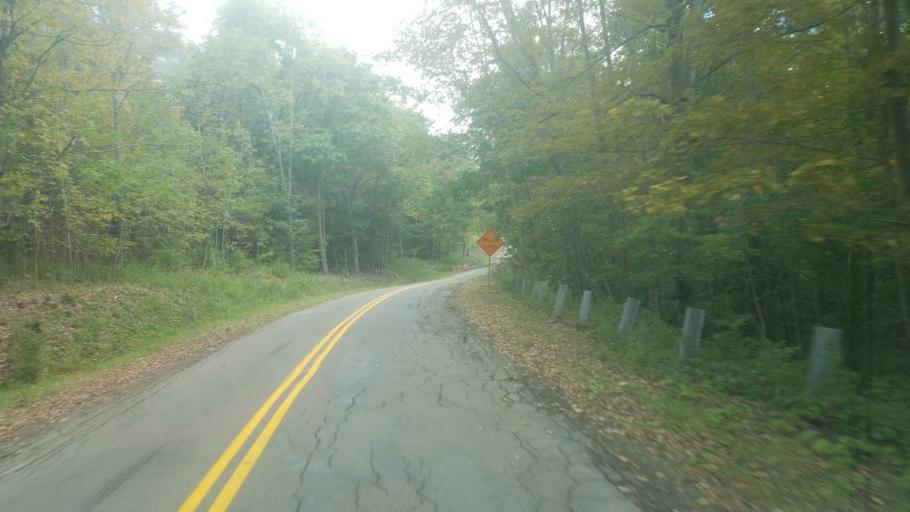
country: US
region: New York
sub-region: Allegany County
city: Cuba
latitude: 42.2223
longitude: -78.3590
